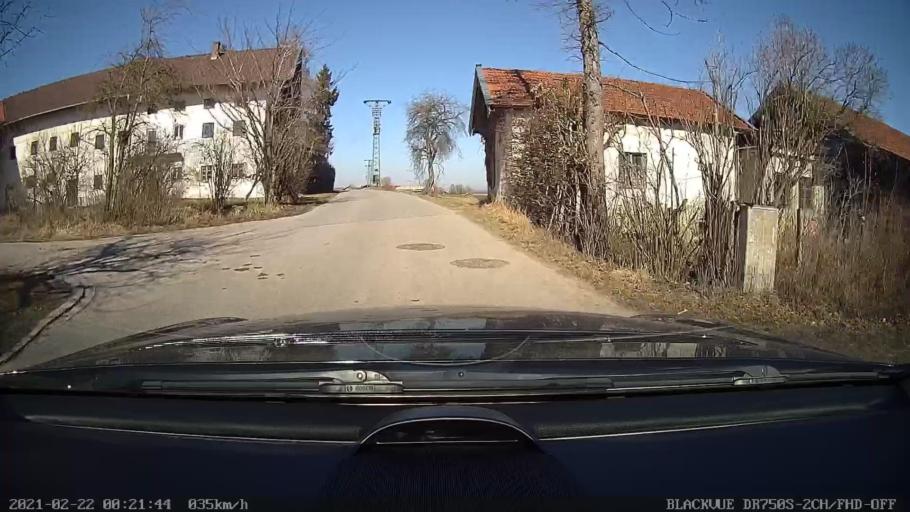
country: DE
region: Bavaria
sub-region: Upper Bavaria
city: Griesstatt
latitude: 47.9806
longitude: 12.1975
